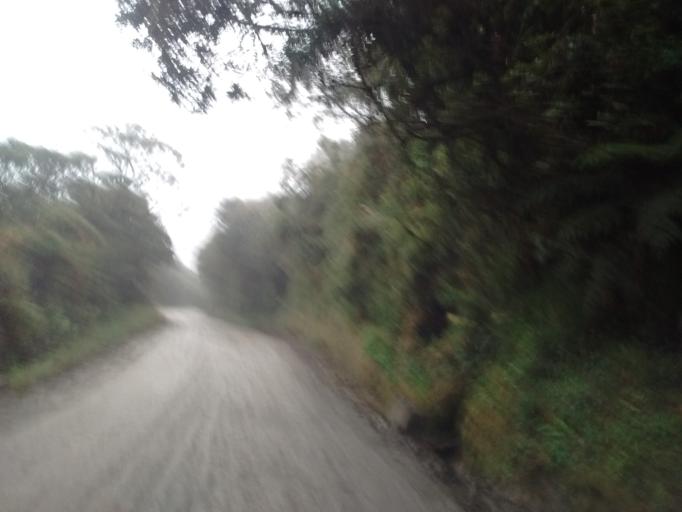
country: CO
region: Cauca
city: Paispamba
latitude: 2.1528
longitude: -76.4498
